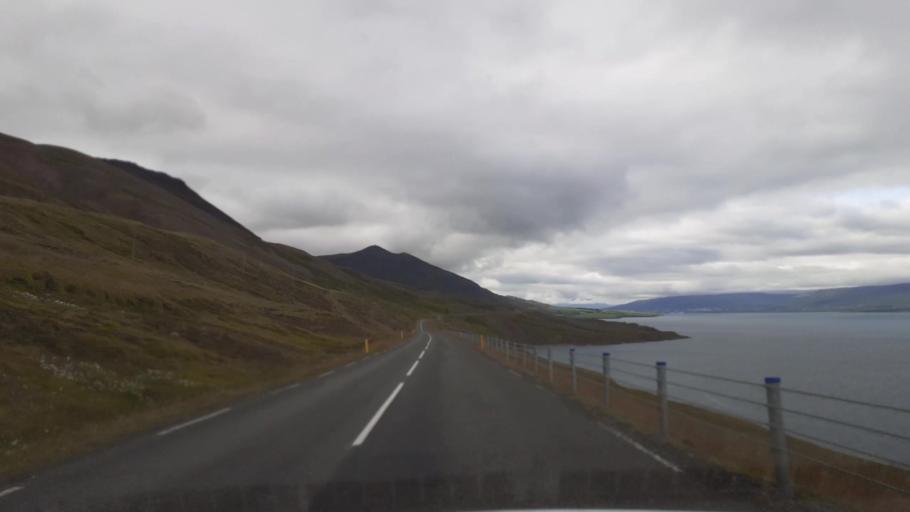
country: IS
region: Northeast
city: Akureyri
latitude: 65.8485
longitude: -18.0597
